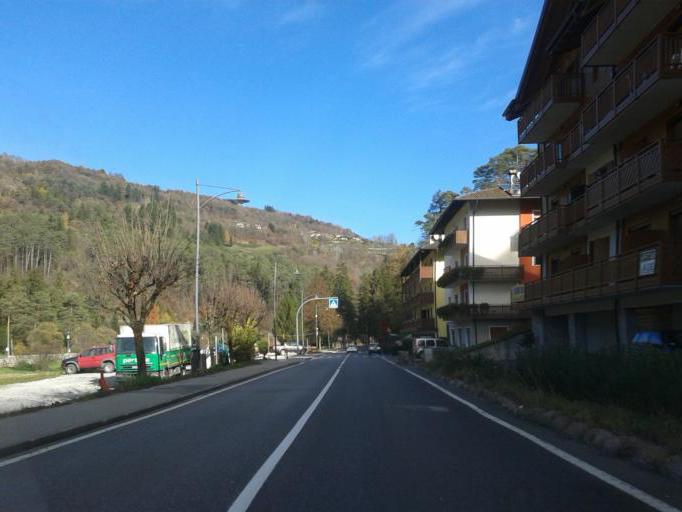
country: IT
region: Trentino-Alto Adige
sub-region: Provincia di Trento
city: Ponte Arche
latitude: 46.0393
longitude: 10.8777
